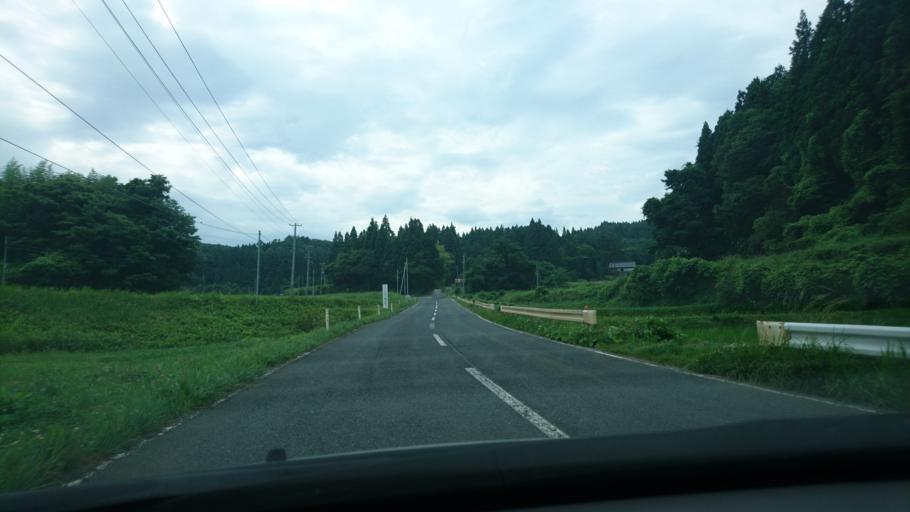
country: JP
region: Iwate
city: Ichinoseki
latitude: 38.8878
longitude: 141.4236
